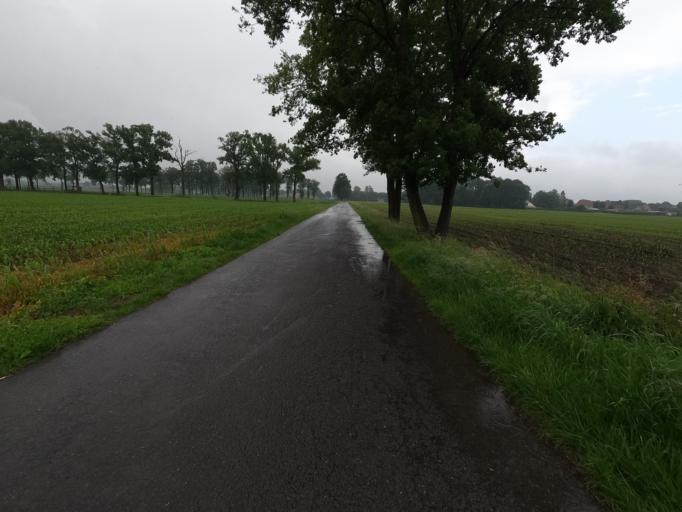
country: BE
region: Flanders
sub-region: Provincie Antwerpen
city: Kalmthout
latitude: 51.3962
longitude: 4.5110
